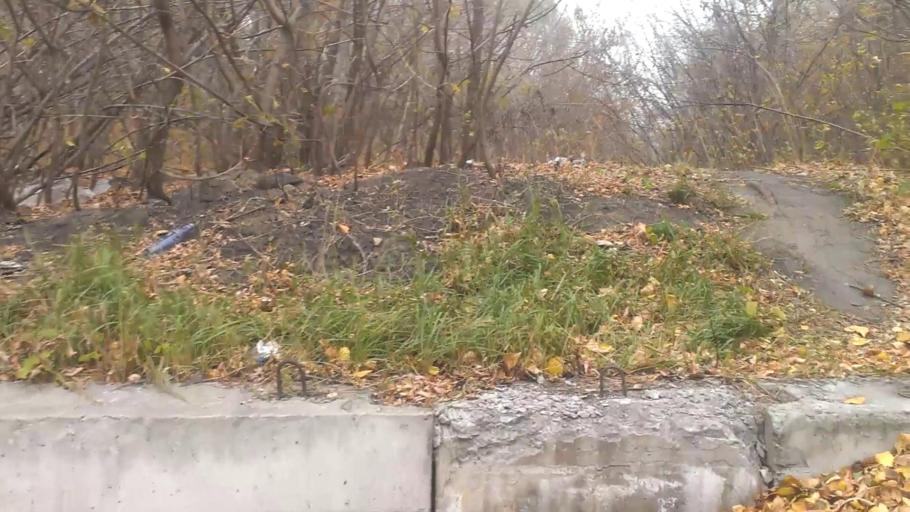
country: RU
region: Altai Krai
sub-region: Gorod Barnaulskiy
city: Barnaul
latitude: 53.3672
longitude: 83.7193
